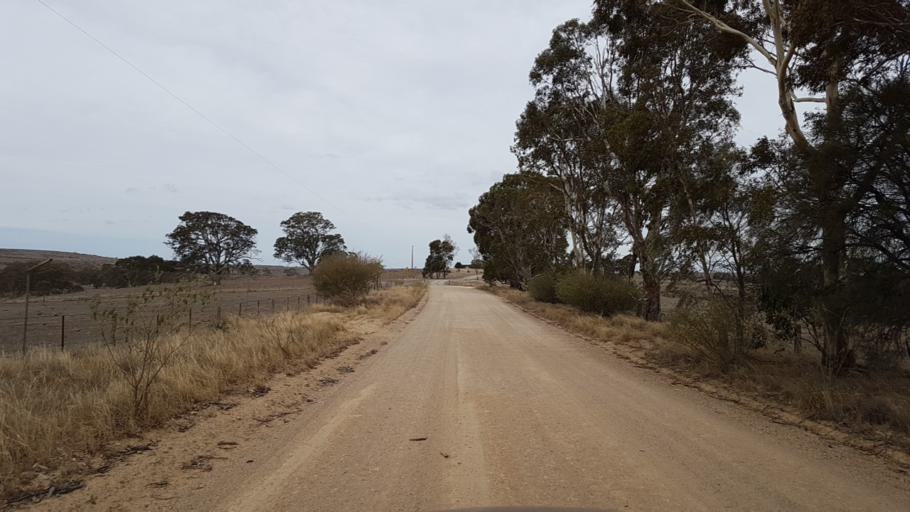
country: AU
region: South Australia
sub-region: Adelaide Hills
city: Birdwood
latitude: -34.8756
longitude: 139.0829
